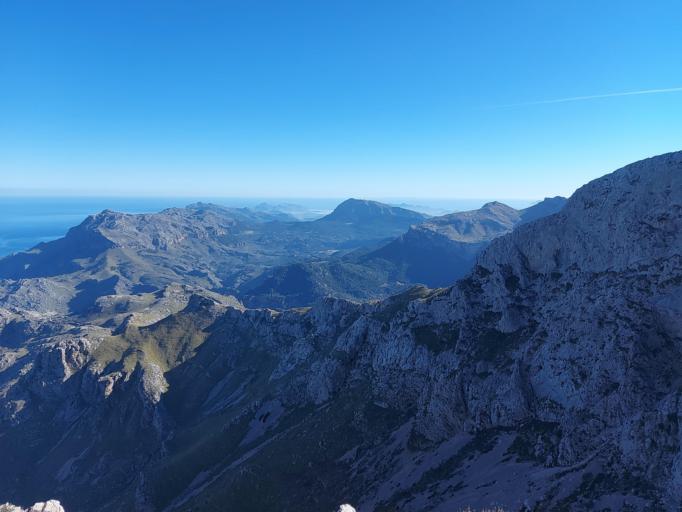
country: ES
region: Balearic Islands
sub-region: Illes Balears
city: Fornalutx
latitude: 39.8132
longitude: 2.7947
